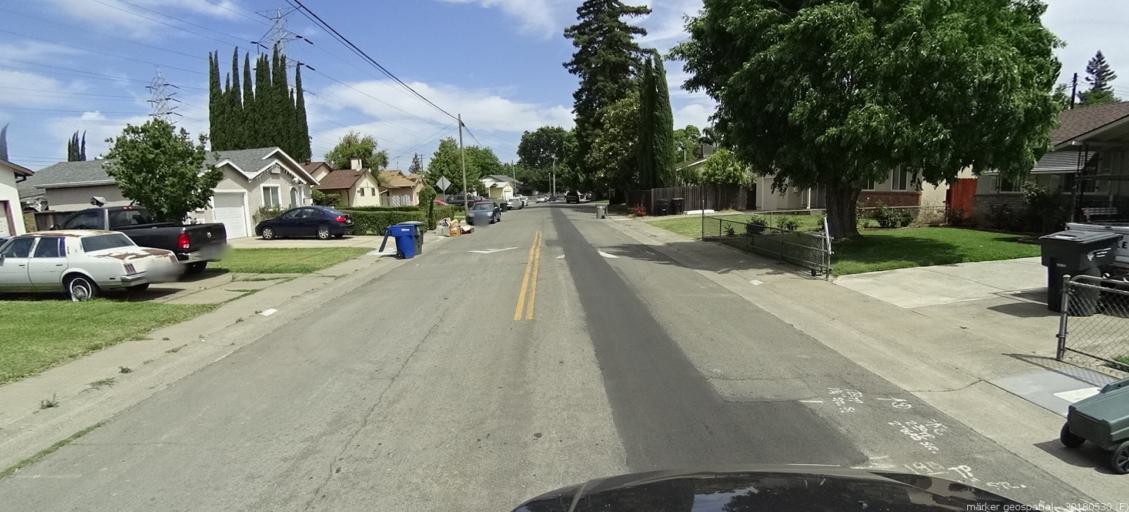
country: US
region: California
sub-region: Sacramento County
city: Sacramento
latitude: 38.6148
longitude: -121.4832
